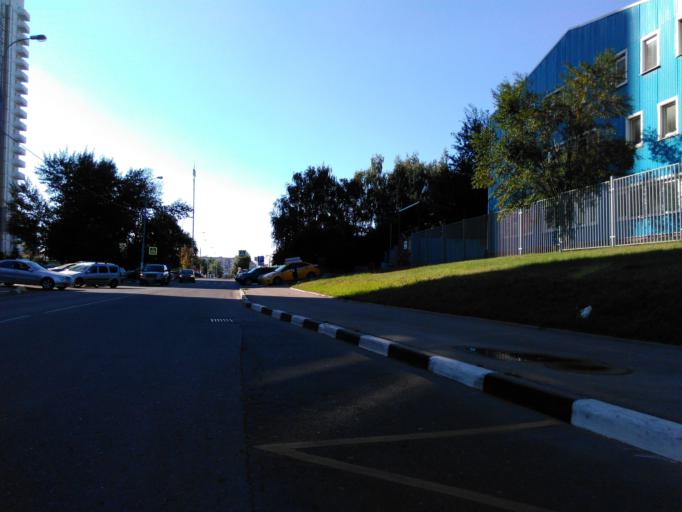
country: RU
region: Moscow
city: Troparevo
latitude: 55.6482
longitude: 37.5017
